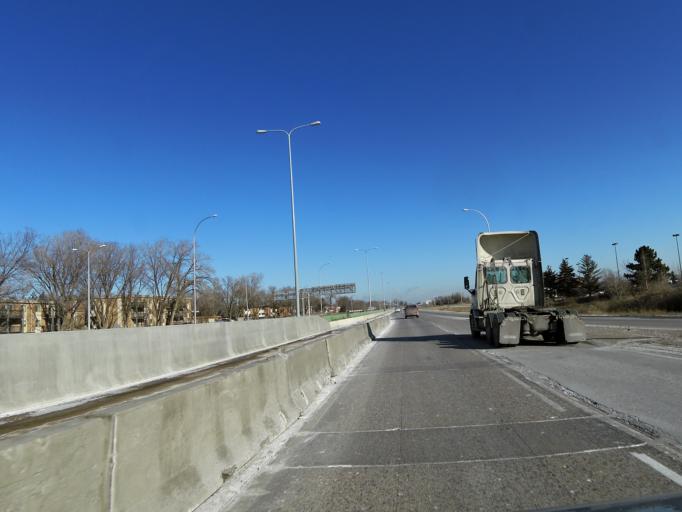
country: US
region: Minnesota
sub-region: Hennepin County
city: Richfield
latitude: 44.8654
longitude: -93.2473
